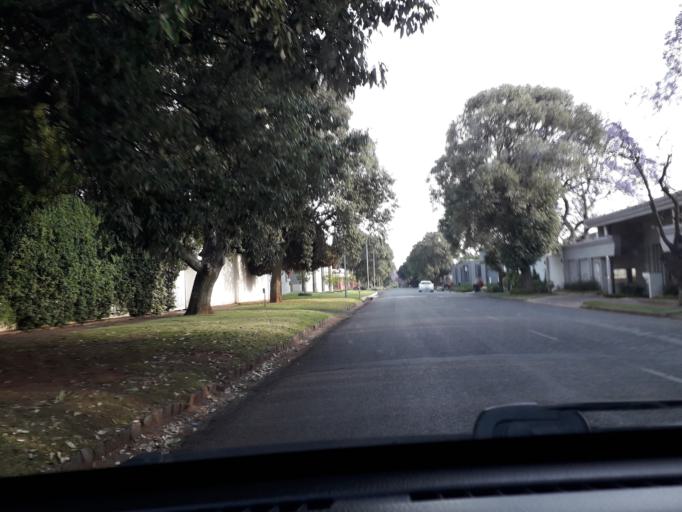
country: ZA
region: Gauteng
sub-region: City of Johannesburg Metropolitan Municipality
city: Johannesburg
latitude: -26.1610
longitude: 28.0651
